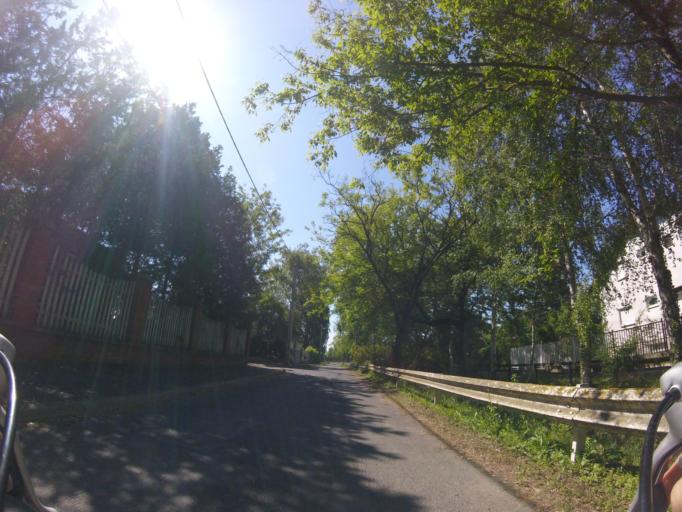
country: HU
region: Somogy
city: Zamardi
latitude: 46.8839
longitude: 17.9552
